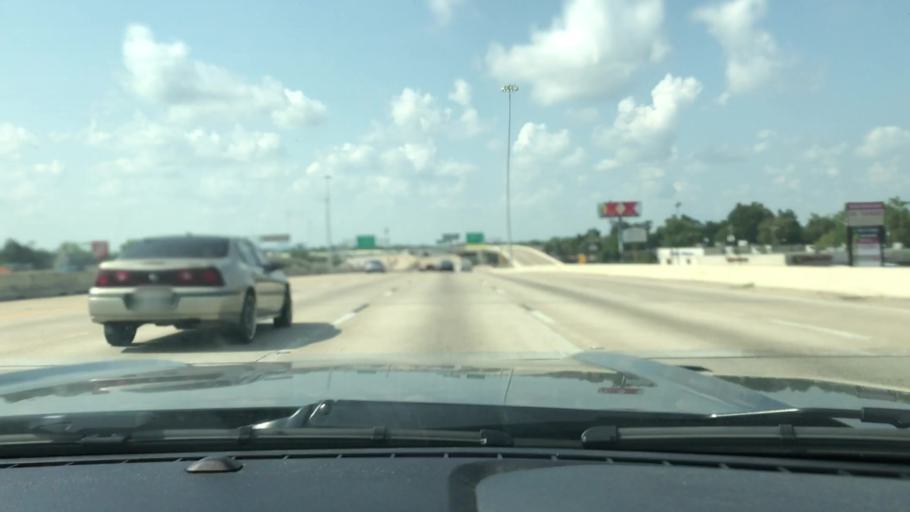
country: US
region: Texas
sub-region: Harris County
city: Aldine
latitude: 29.8699
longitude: -95.3304
